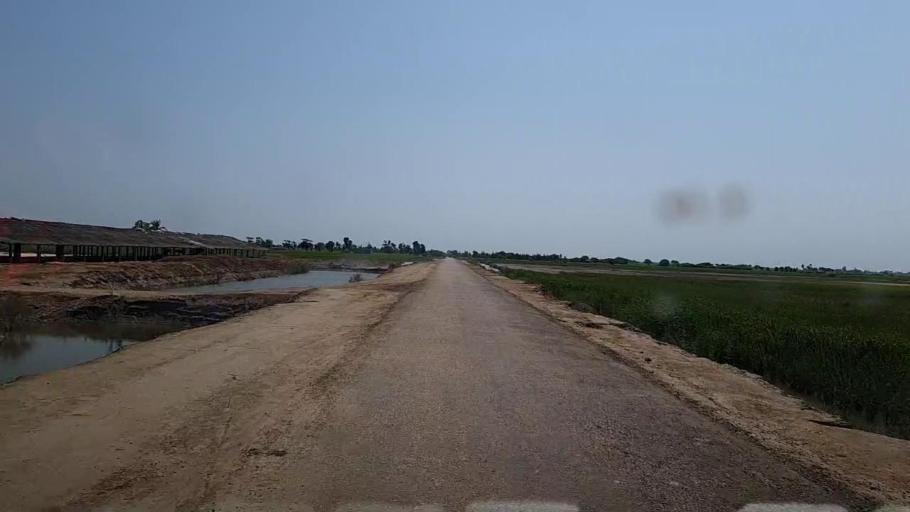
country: PK
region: Sindh
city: Mirpur Batoro
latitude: 24.6209
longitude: 68.4523
